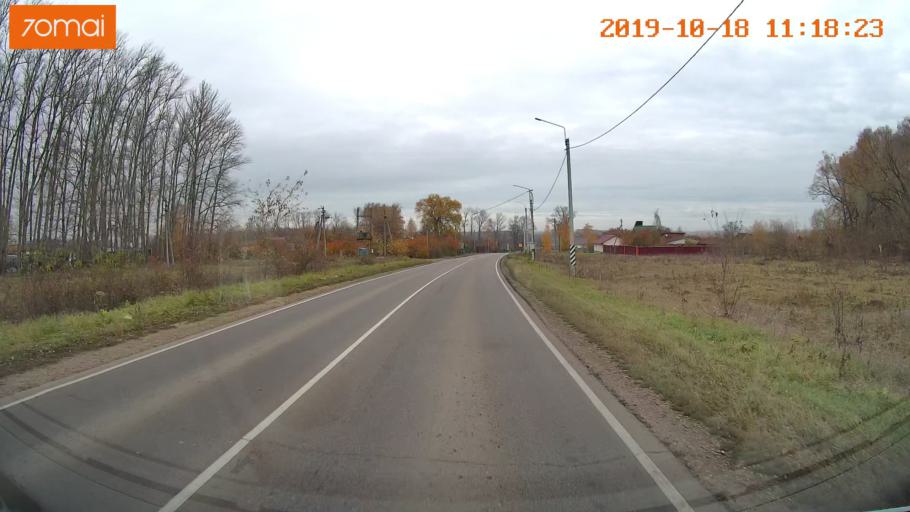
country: RU
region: Tula
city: Kimovsk
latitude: 54.0385
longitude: 38.5502
